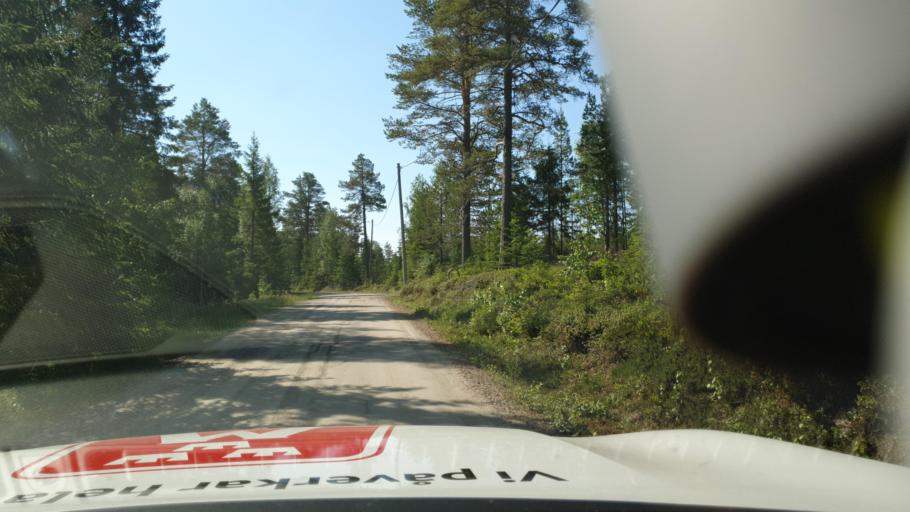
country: SE
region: Vaesterbotten
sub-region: Robertsfors Kommun
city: Robertsfors
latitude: 64.2149
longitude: 21.0776
